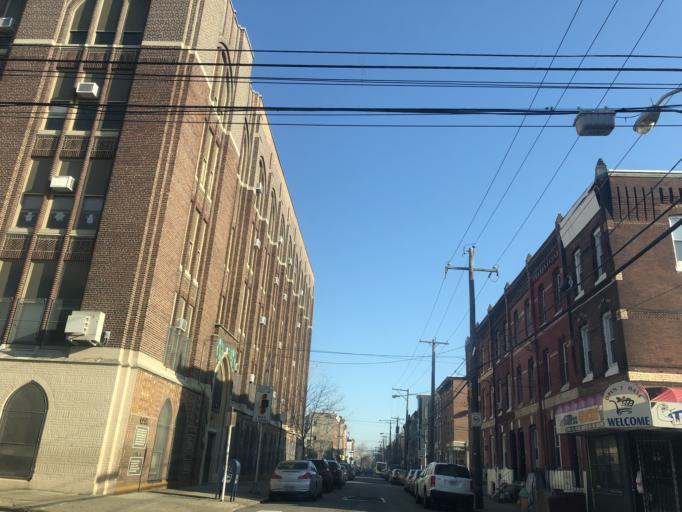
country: US
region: Pennsylvania
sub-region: Philadelphia County
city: Philadelphia
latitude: 39.9346
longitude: -75.1710
